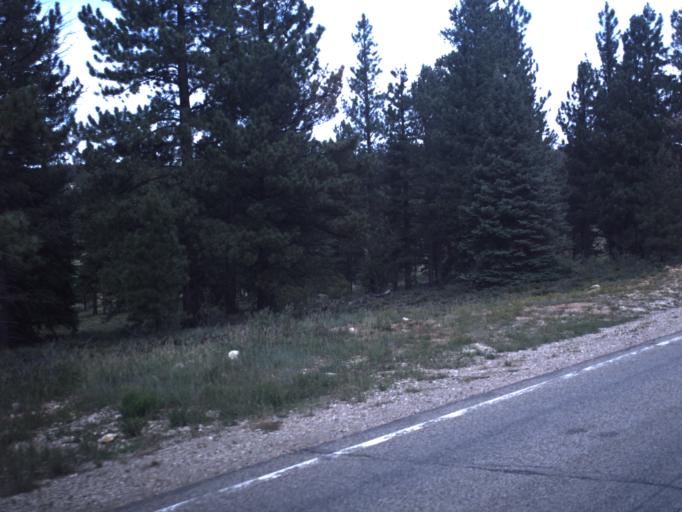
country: US
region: Utah
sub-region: Garfield County
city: Panguitch
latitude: 37.5006
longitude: -112.6227
